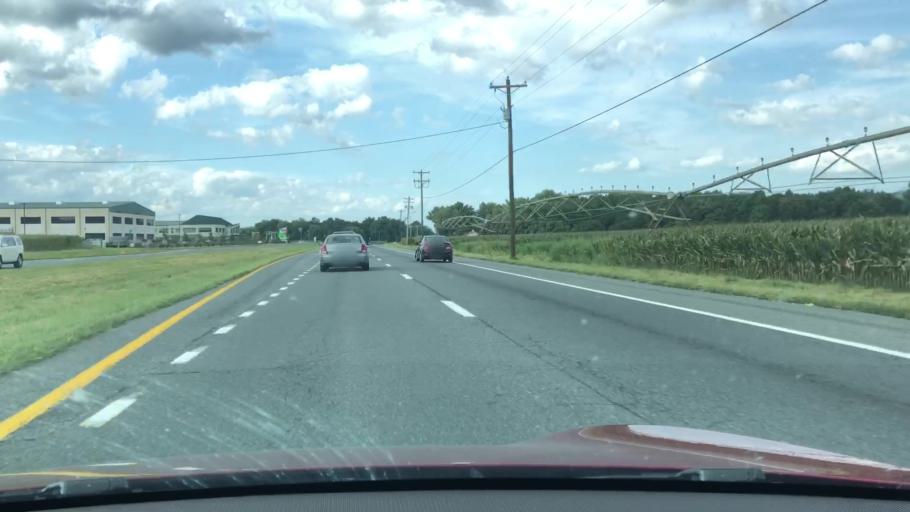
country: US
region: Delaware
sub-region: Sussex County
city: Bridgeville
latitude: 38.7884
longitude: -75.5897
